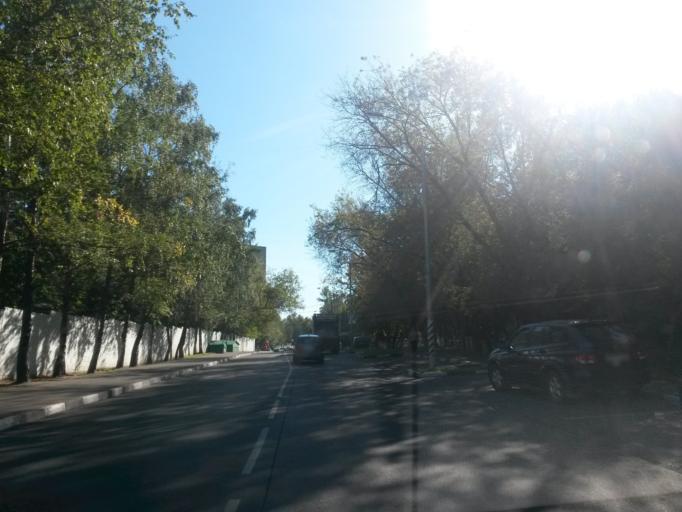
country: RU
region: Moscow
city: Zyuzino
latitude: 55.6542
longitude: 37.5822
